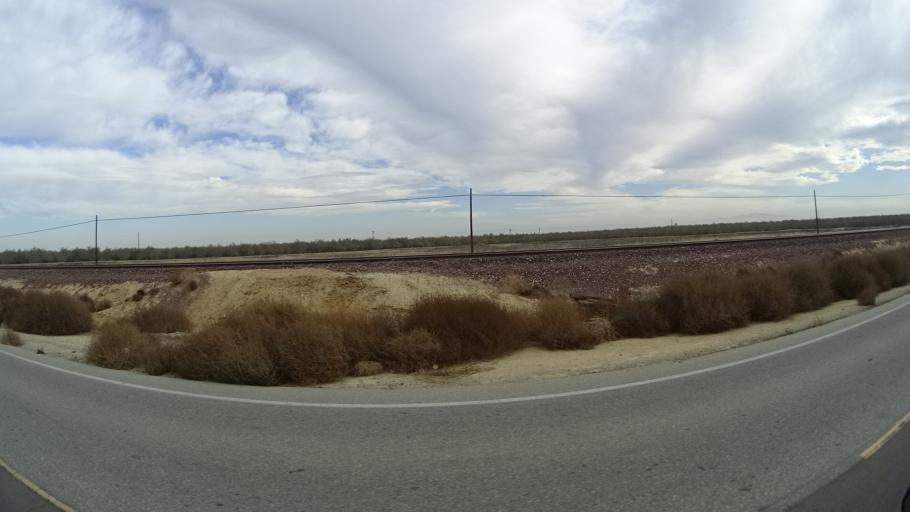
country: US
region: California
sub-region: Kern County
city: Rosedale
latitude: 35.4328
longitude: -119.1884
